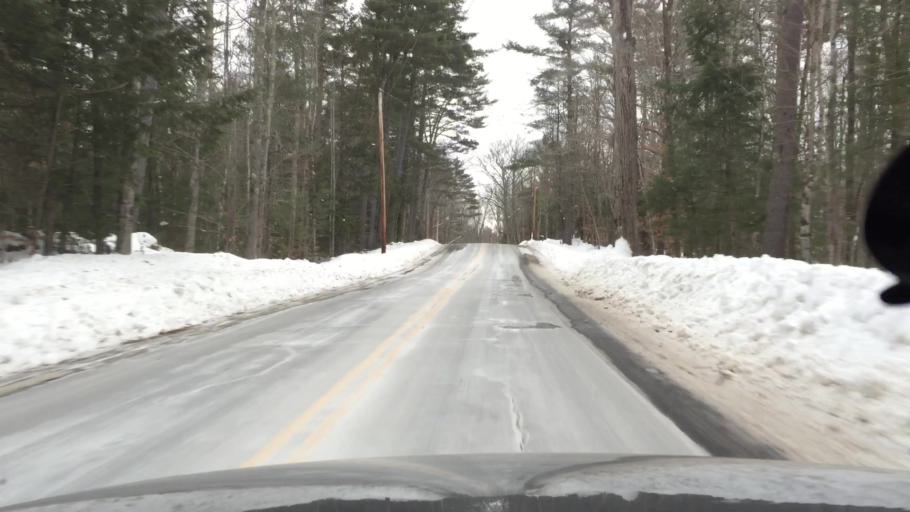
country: US
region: New Hampshire
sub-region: Grafton County
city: Holderness
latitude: 43.7937
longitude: -71.5141
